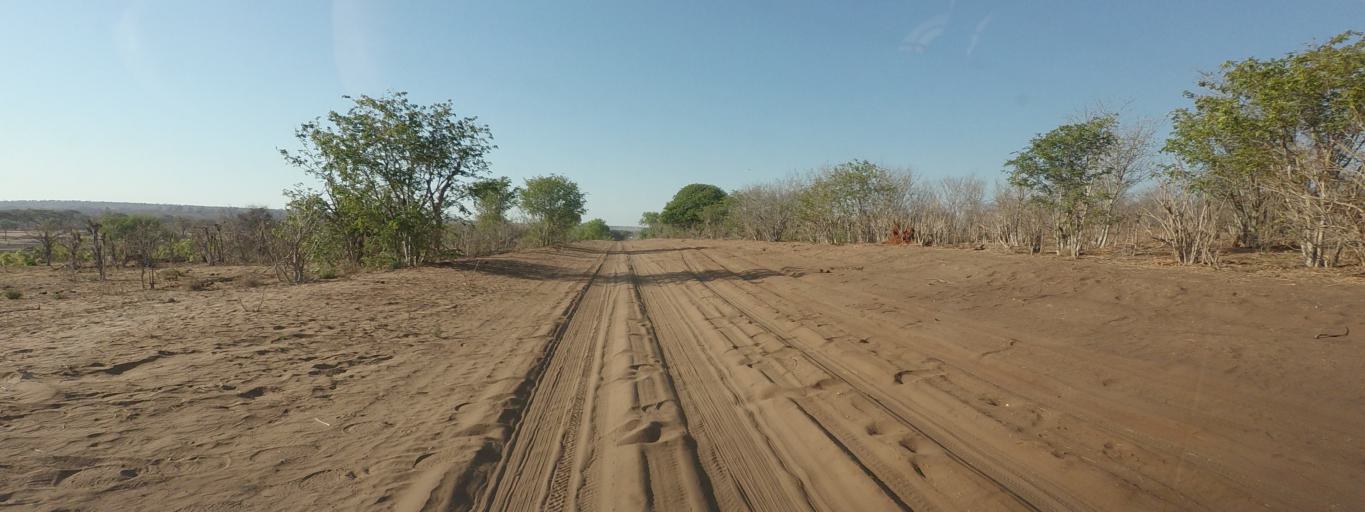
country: BW
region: North West
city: Kasane
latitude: -17.8739
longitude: 25.2343
